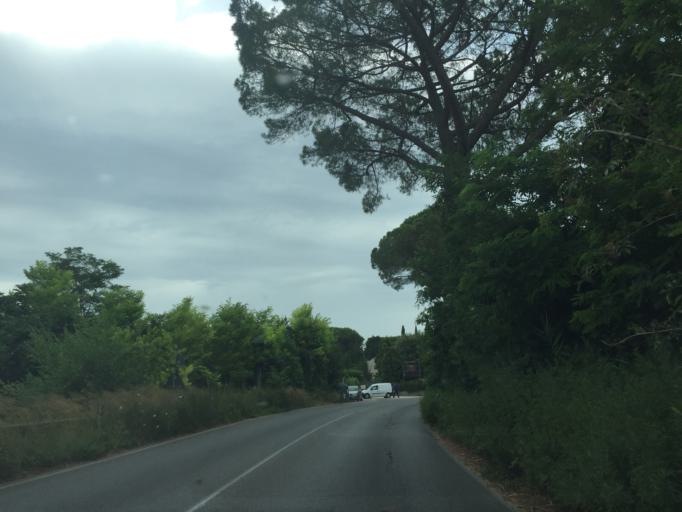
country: IT
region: Tuscany
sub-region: Province of Pisa
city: Uliveto Terme
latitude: 43.6910
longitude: 10.5271
